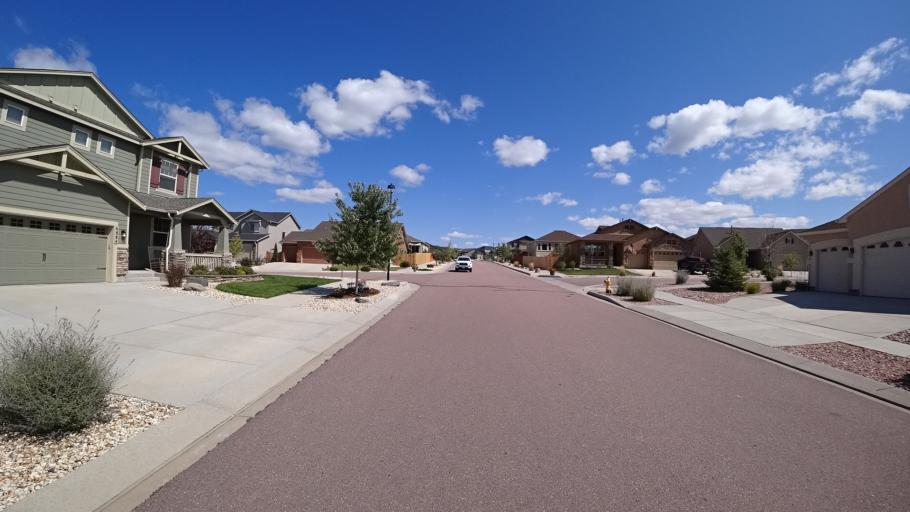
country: US
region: Colorado
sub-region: El Paso County
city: Cimarron Hills
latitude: 38.9309
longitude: -104.6853
